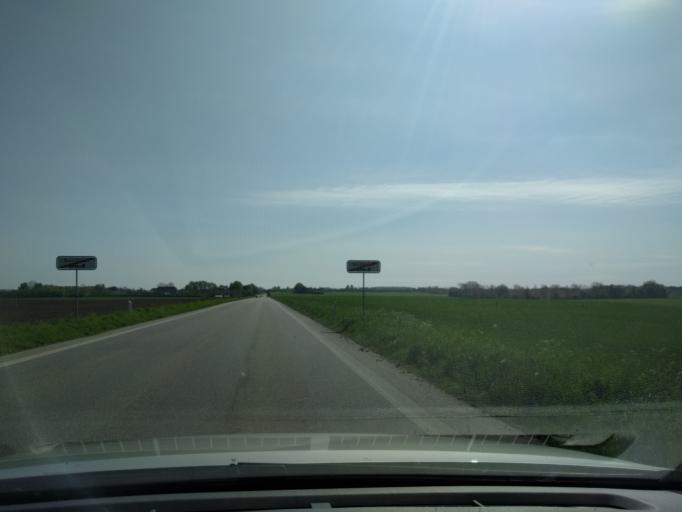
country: DK
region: Zealand
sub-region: Guldborgsund Kommune
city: Norre Alslev
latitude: 54.8983
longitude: 11.9469
